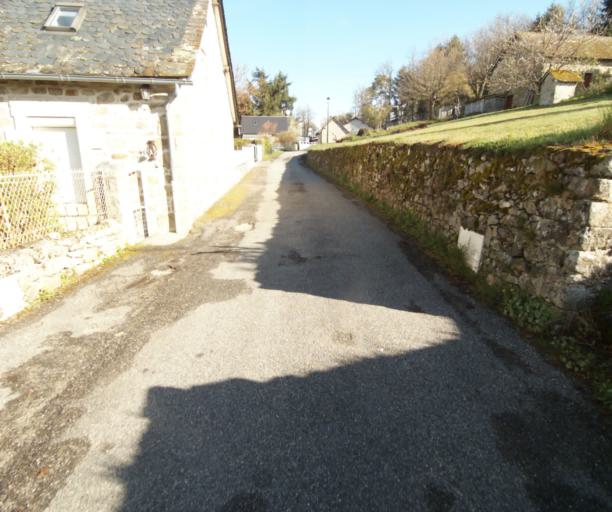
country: FR
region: Limousin
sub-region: Departement de la Correze
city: Laguenne
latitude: 45.2674
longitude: 1.8738
